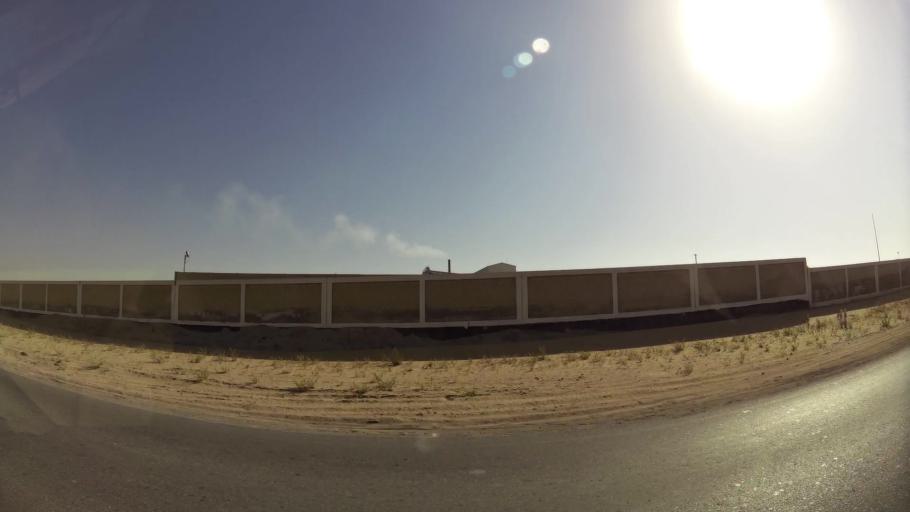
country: AE
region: Dubai
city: Dubai
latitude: 24.9982
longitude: 55.1232
